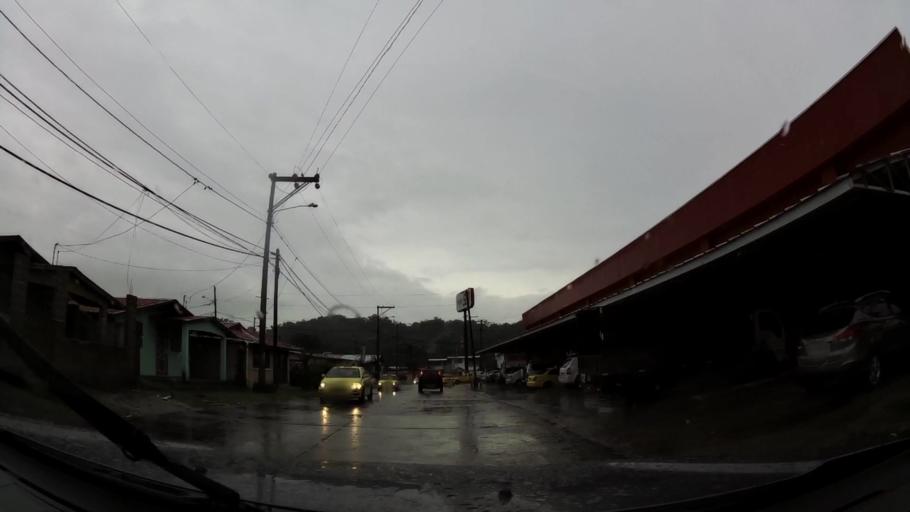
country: PA
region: Colon
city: Sabanitas
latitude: 9.3492
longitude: -79.8090
